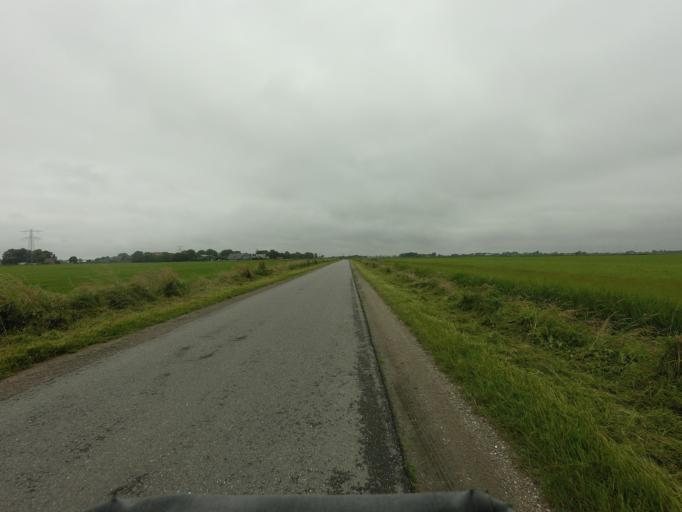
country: NL
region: North Holland
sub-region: Gemeente Schagen
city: Schagen
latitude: 52.7690
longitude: 4.8330
